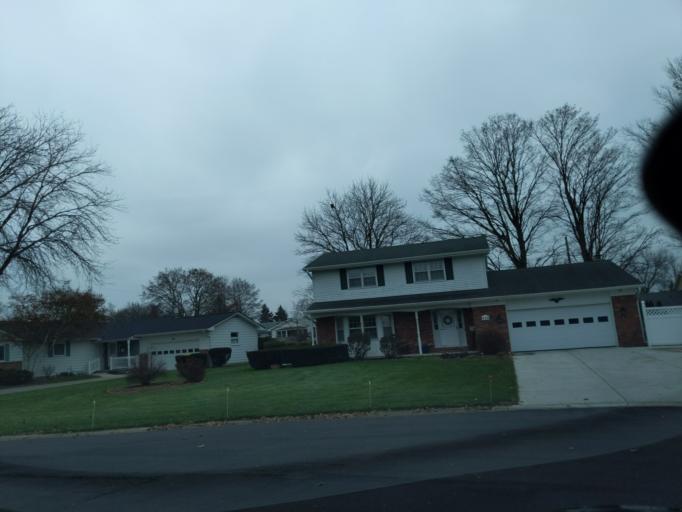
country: US
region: Michigan
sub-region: Eaton County
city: Waverly
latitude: 42.7287
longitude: -84.6306
